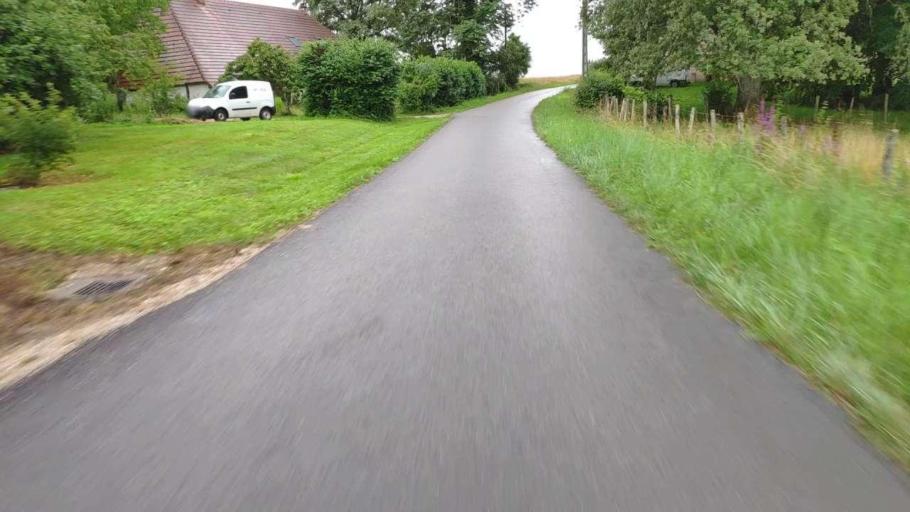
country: FR
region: Franche-Comte
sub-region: Departement du Jura
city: Chaussin
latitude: 46.8793
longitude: 5.4150
